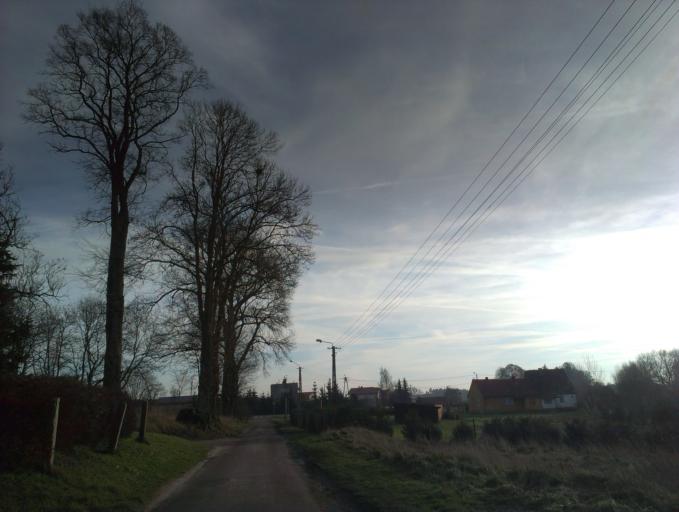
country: PL
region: Pomeranian Voivodeship
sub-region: Powiat czluchowski
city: Debrzno
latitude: 53.6152
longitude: 17.1870
